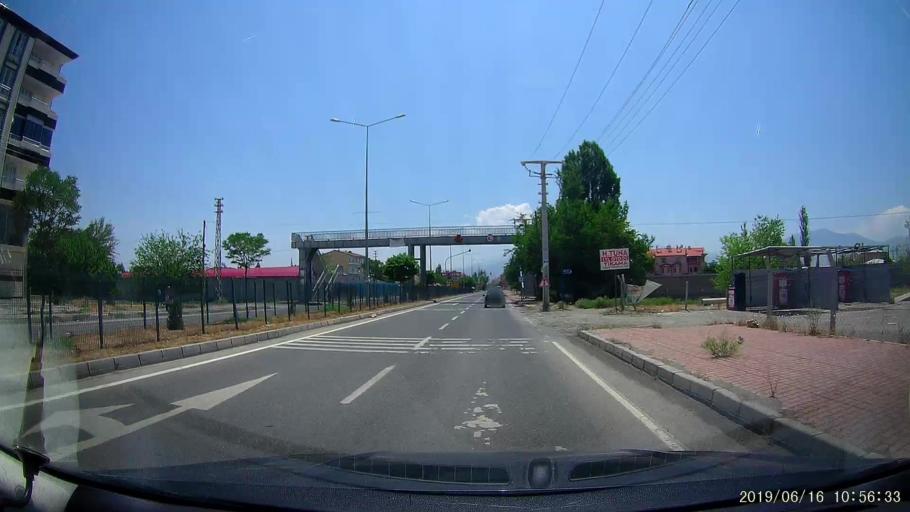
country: TR
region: Igdir
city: Igdir
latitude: 39.9286
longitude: 44.0244
